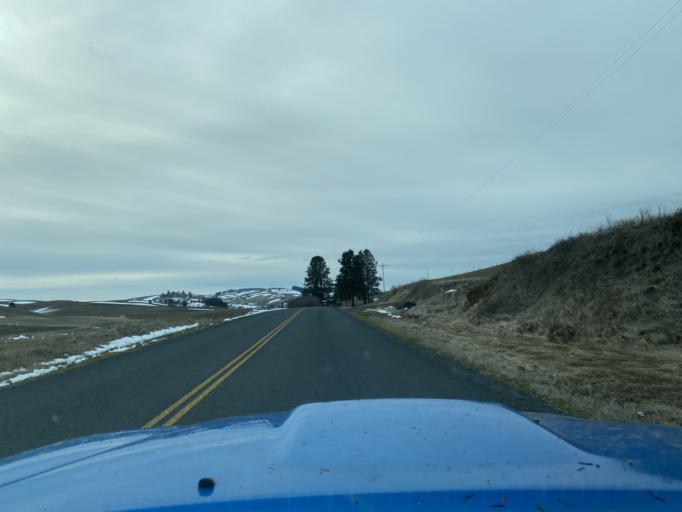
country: US
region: Idaho
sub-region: Latah County
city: Moscow
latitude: 46.6878
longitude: -116.8856
